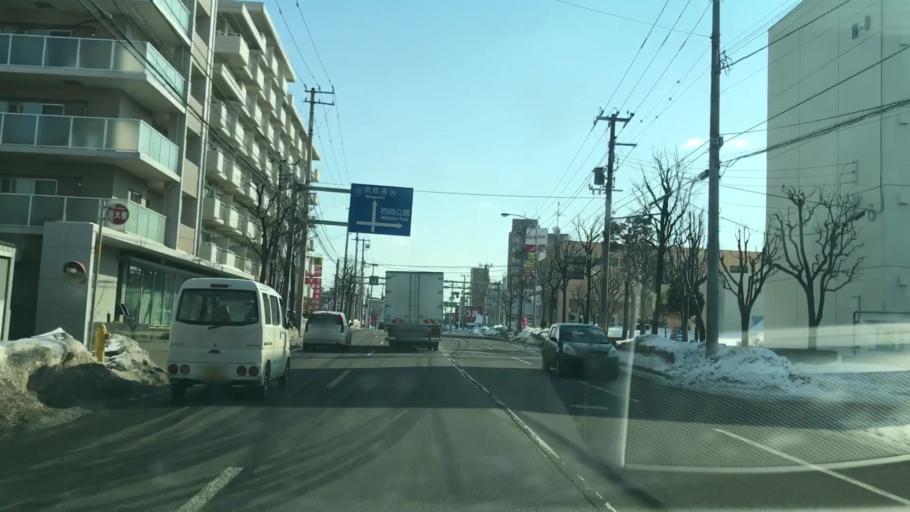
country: JP
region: Hokkaido
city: Sapporo
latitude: 43.0238
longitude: 141.3901
